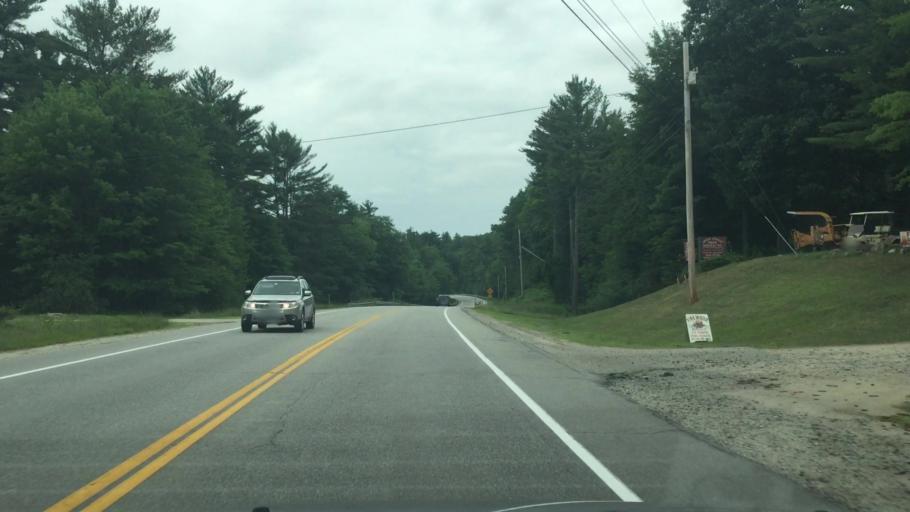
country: US
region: New Hampshire
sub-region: Carroll County
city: Moultonborough
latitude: 43.7770
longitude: -71.3815
